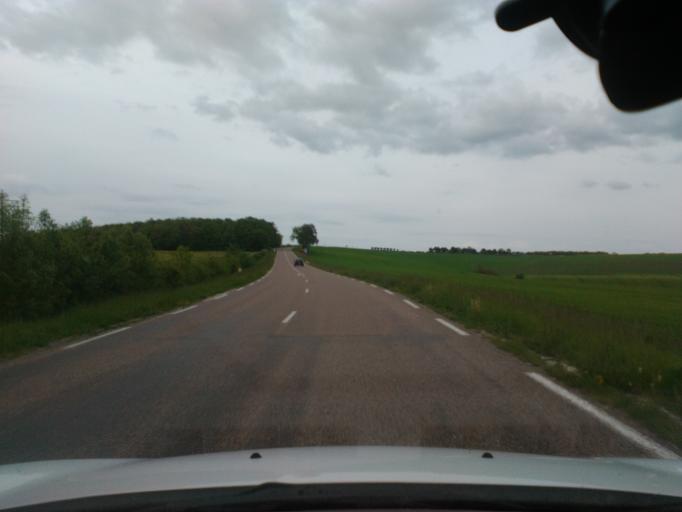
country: FR
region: Champagne-Ardenne
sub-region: Departement de la Haute-Marne
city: Lavilleneuve-au-Roi
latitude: 48.2253
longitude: 4.8601
